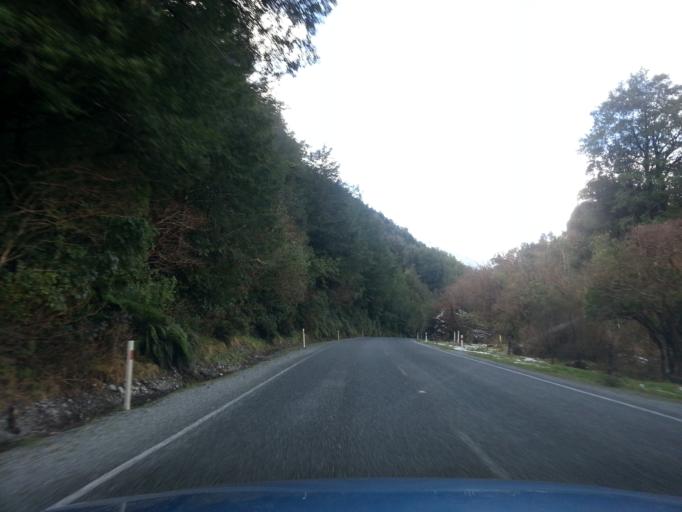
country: NZ
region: West Coast
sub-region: Grey District
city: Greymouth
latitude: -42.7798
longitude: 171.6132
